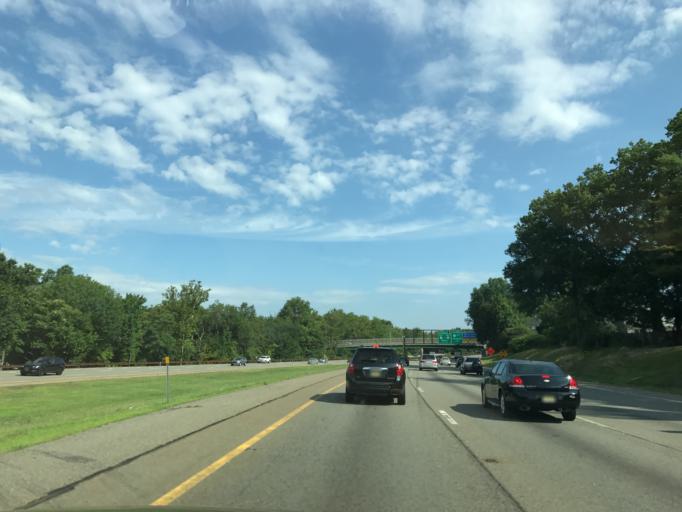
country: US
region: New Jersey
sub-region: Essex County
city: Brookdale
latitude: 40.8311
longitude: -74.1780
